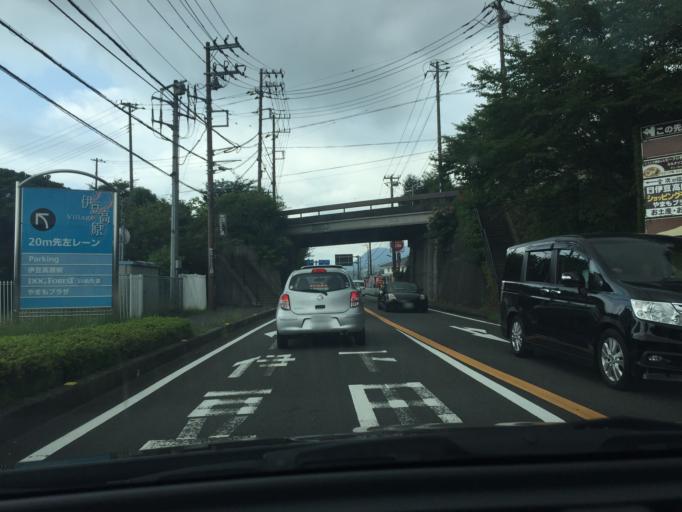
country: JP
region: Shizuoka
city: Ito
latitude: 34.8814
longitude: 139.1077
